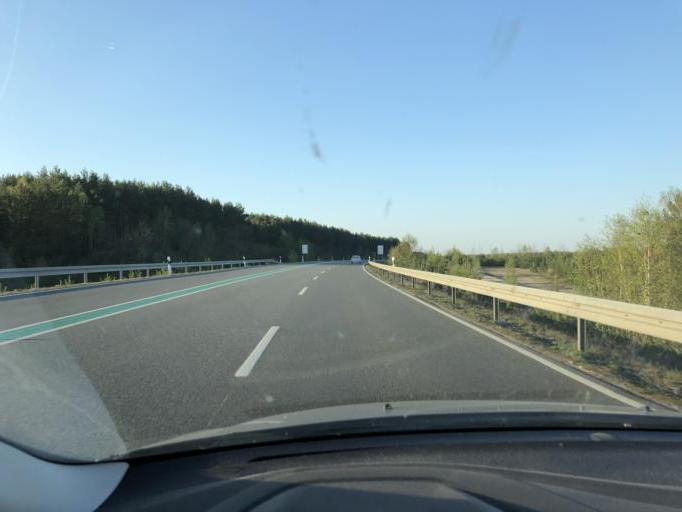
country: DE
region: Brandenburg
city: Senftenberg
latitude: 51.5103
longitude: 13.9568
